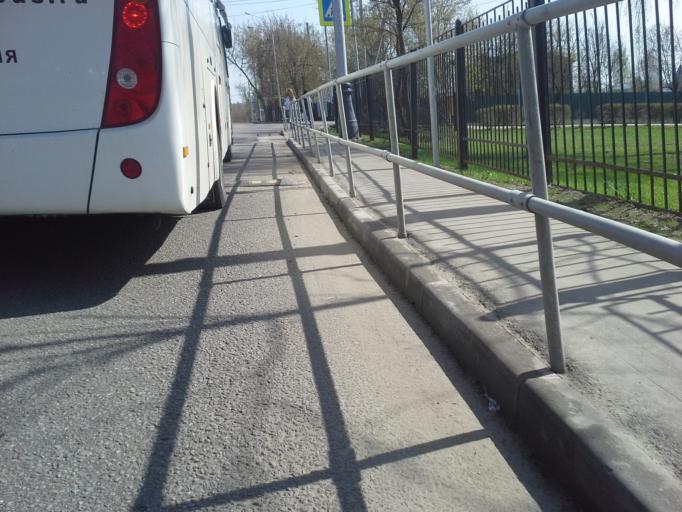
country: RU
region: Moskovskaya
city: Shcherbinka
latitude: 55.4936
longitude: 37.5041
